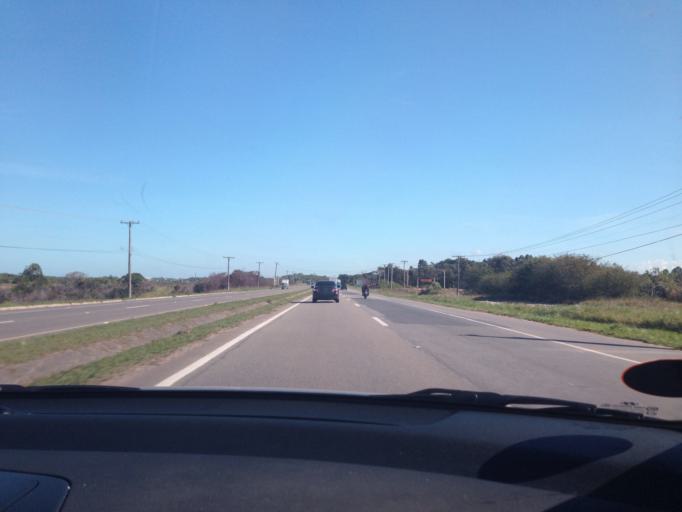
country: BR
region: Espirito Santo
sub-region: Vila Velha
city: Vila Velha
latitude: -20.4552
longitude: -40.3391
